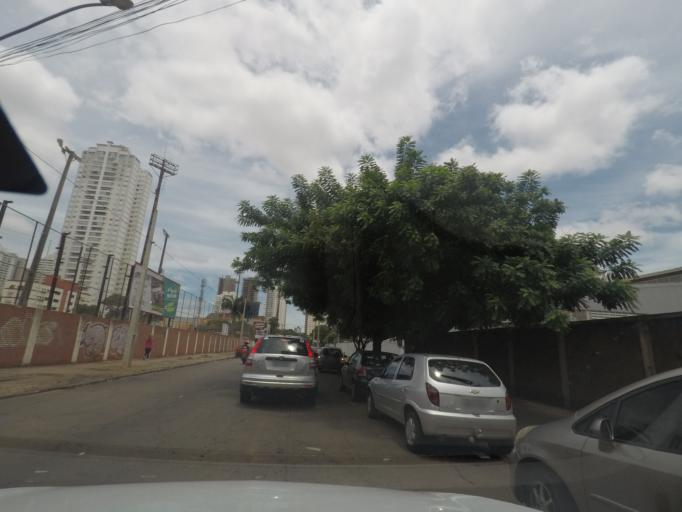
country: BR
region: Goias
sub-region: Goiania
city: Goiania
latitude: -16.6941
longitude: -49.2754
